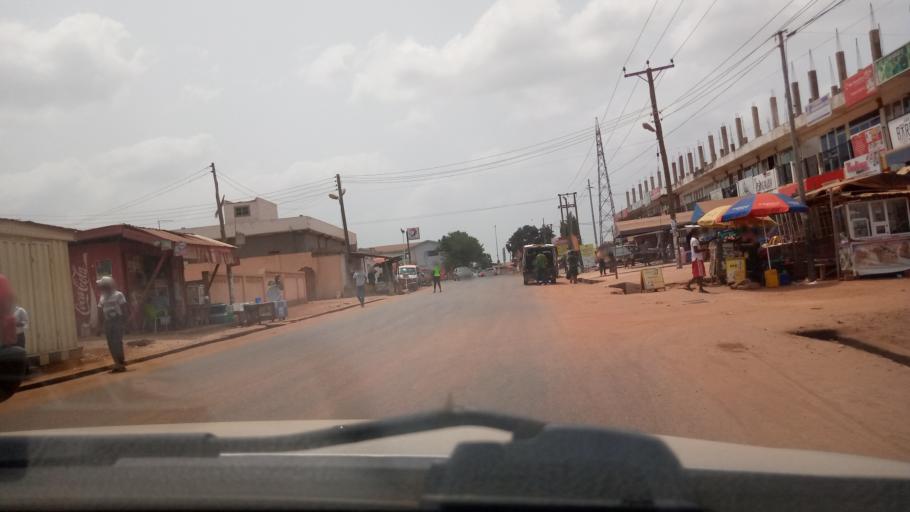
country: GH
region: Greater Accra
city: Dome
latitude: 5.6687
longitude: -0.2057
